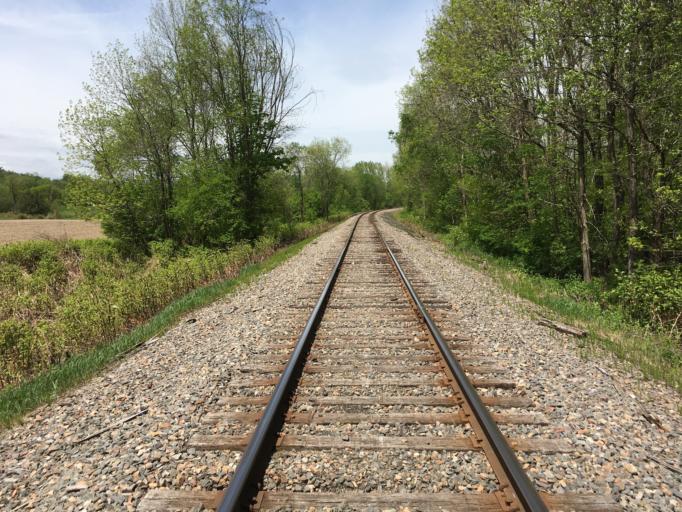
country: US
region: Vermont
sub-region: Windsor County
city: Chester
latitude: 43.2535
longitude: -72.5740
